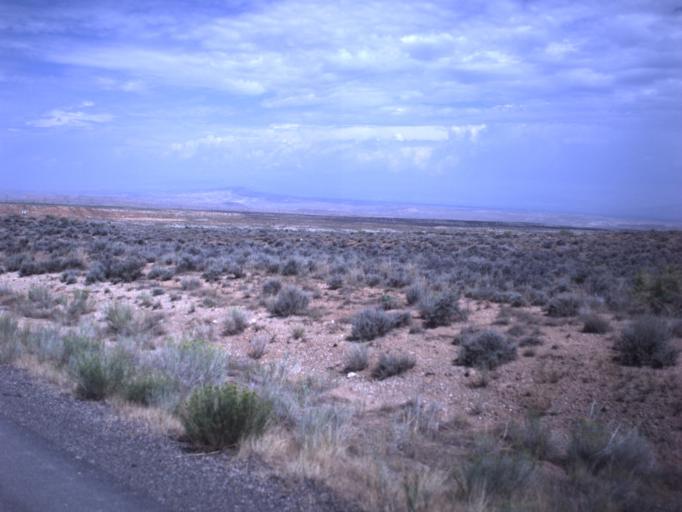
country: US
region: Utah
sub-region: Uintah County
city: Naples
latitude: 40.2086
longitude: -109.3642
